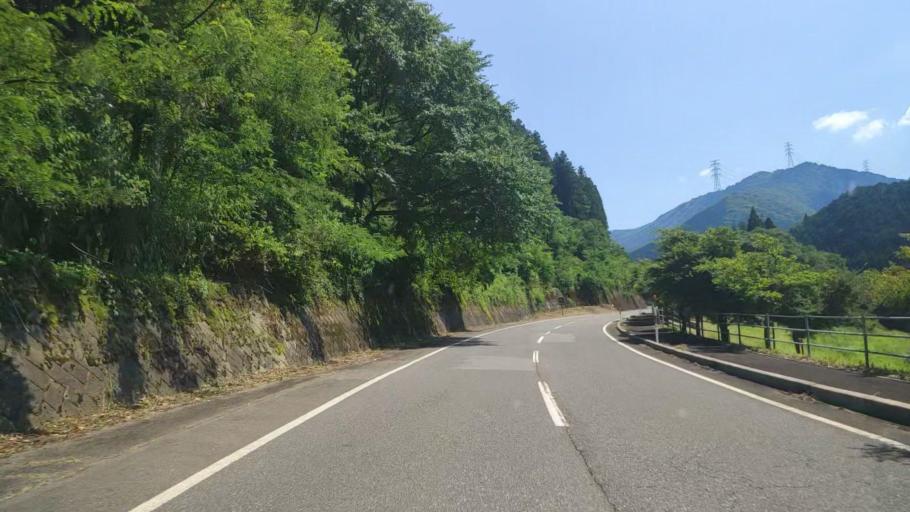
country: JP
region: Gifu
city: Godo
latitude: 35.6003
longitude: 136.6293
